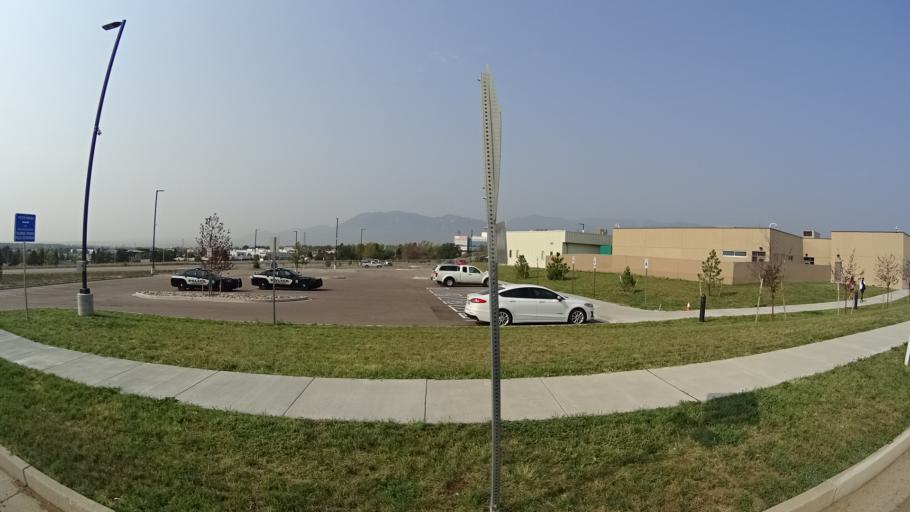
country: US
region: Colorado
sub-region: El Paso County
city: Stratmoor
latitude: 38.8160
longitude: -104.7532
